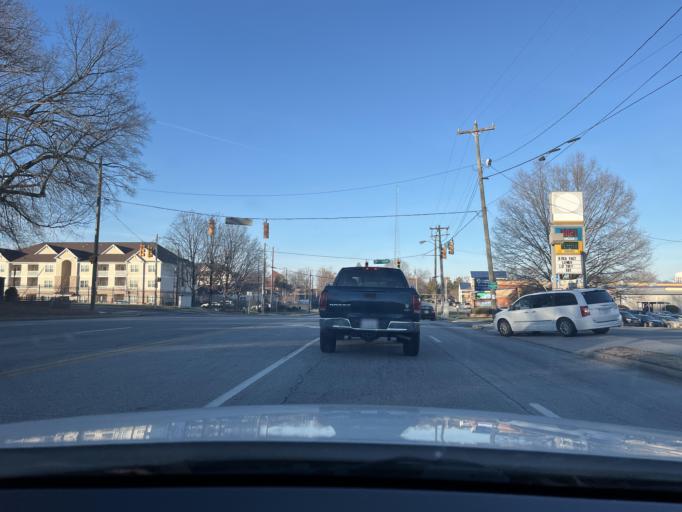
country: US
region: North Carolina
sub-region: Guilford County
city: Greensboro
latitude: 36.0585
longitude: -79.7937
